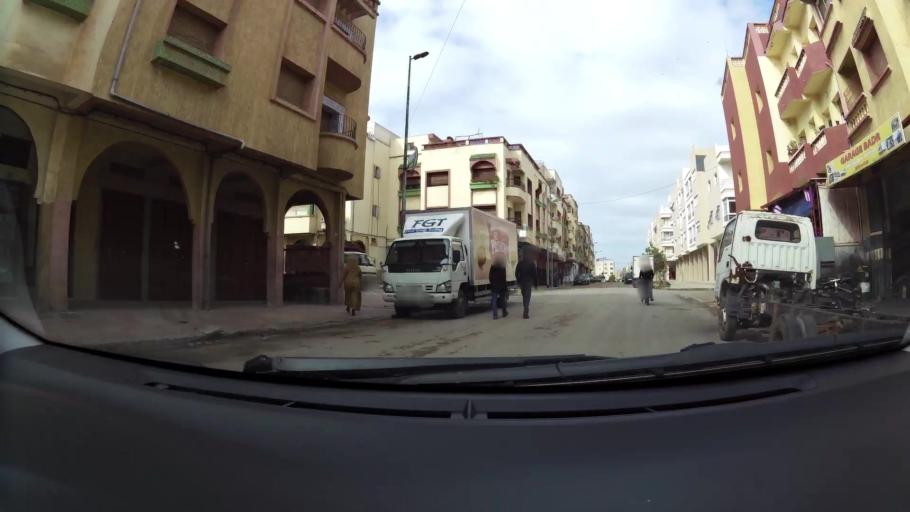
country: MA
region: Grand Casablanca
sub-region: Mohammedia
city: Mohammedia
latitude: 33.6828
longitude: -7.3743
